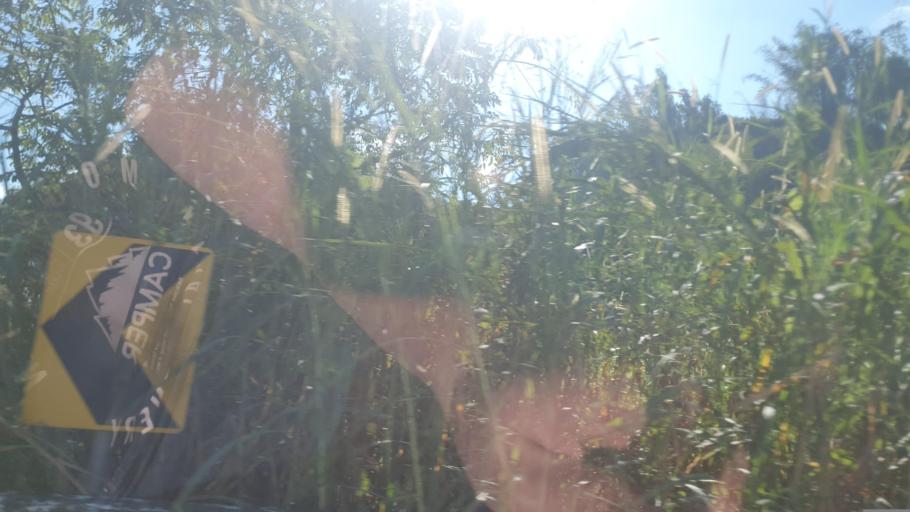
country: TW
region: Taiwan
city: Yujing
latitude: 23.0445
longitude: 120.3990
